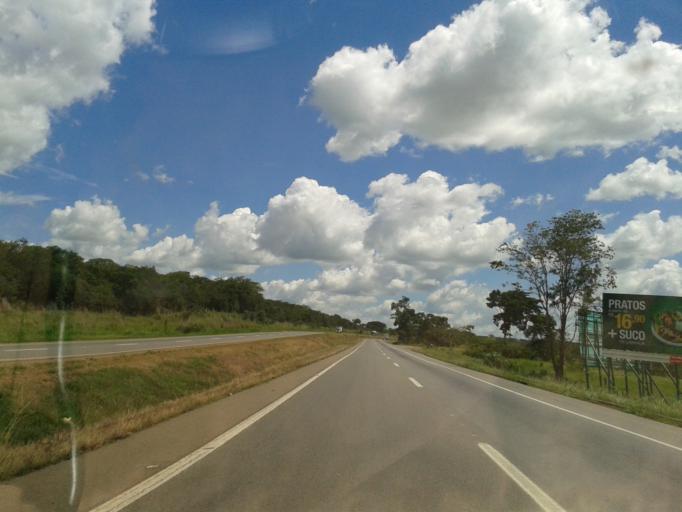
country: BR
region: Goias
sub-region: Hidrolandia
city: Hidrolandia
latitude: -16.9076
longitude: -49.2539
